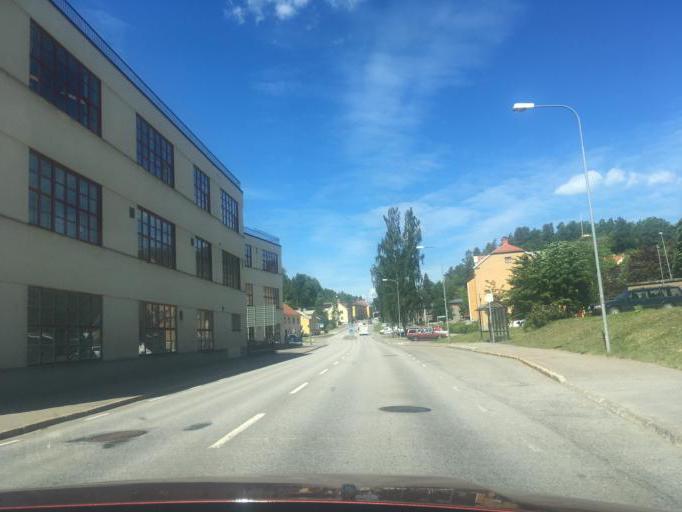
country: SE
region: OEstergoetland
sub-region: Valdemarsviks Kommun
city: Valdemarsvik
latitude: 58.2053
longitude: 16.6012
